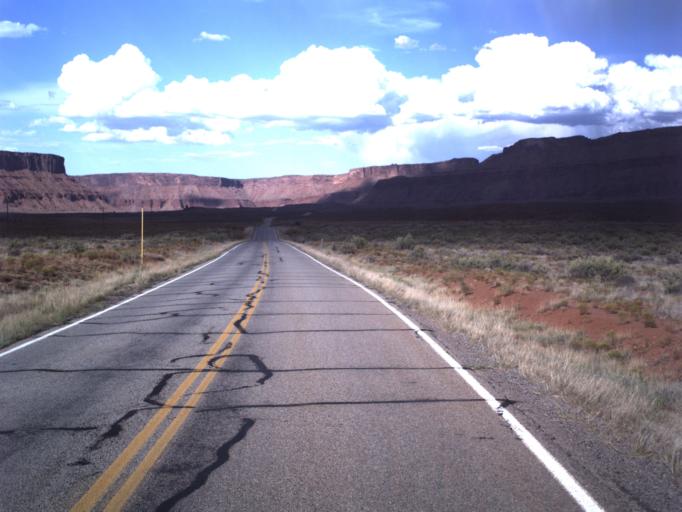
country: US
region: Utah
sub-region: Grand County
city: Moab
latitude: 38.7076
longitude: -109.3804
